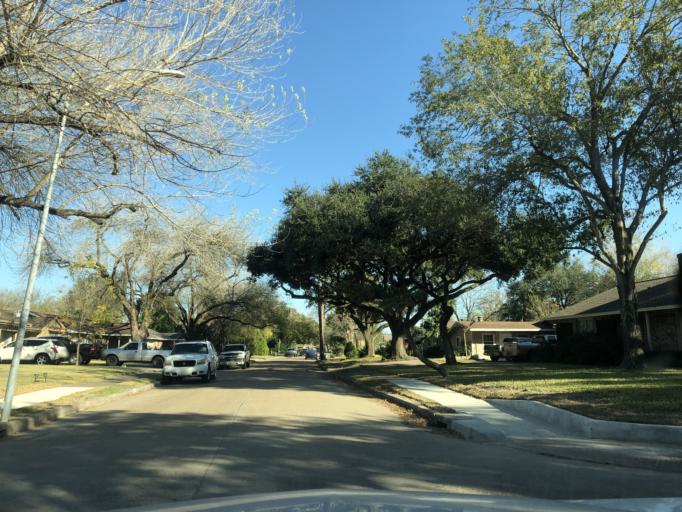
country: US
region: Texas
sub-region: Harris County
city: Bellaire
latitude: 29.6972
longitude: -95.5089
